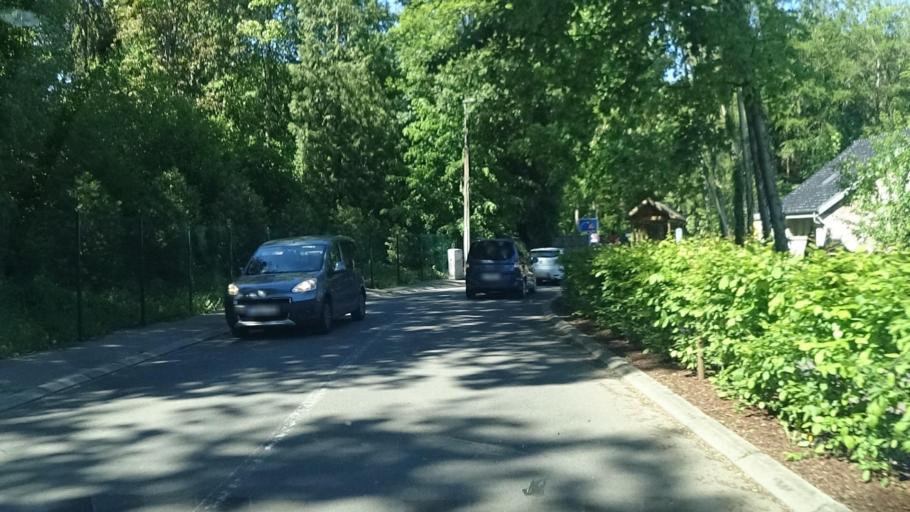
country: BE
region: Wallonia
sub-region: Province du Brabant Wallon
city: Court-Saint-Etienne
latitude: 50.6425
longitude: 4.5760
